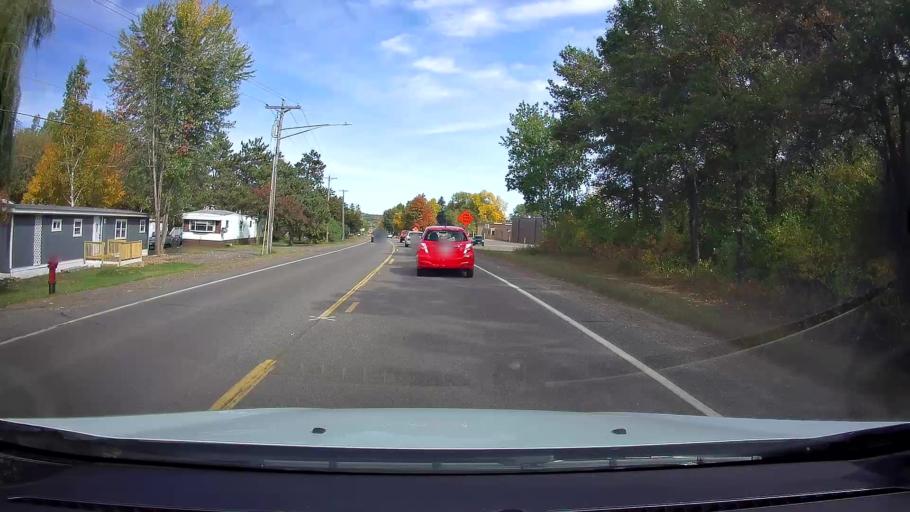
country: US
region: Wisconsin
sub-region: Polk County
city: Saint Croix Falls
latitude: 45.3511
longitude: -92.6380
